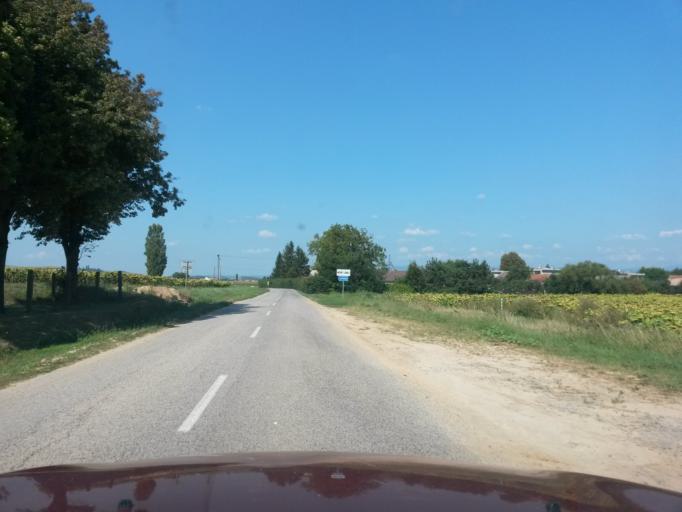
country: SK
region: Kosicky
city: Moldava nad Bodvou
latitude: 48.5322
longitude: 21.1125
